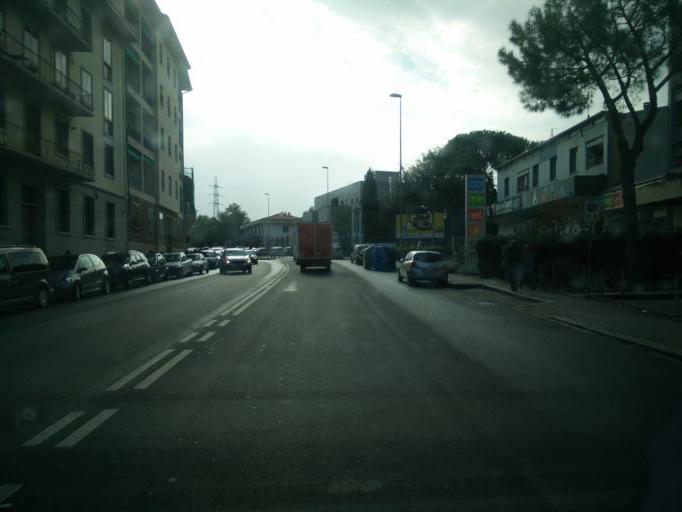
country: IT
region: Tuscany
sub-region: Province of Florence
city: Florence
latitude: 43.7881
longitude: 11.2248
